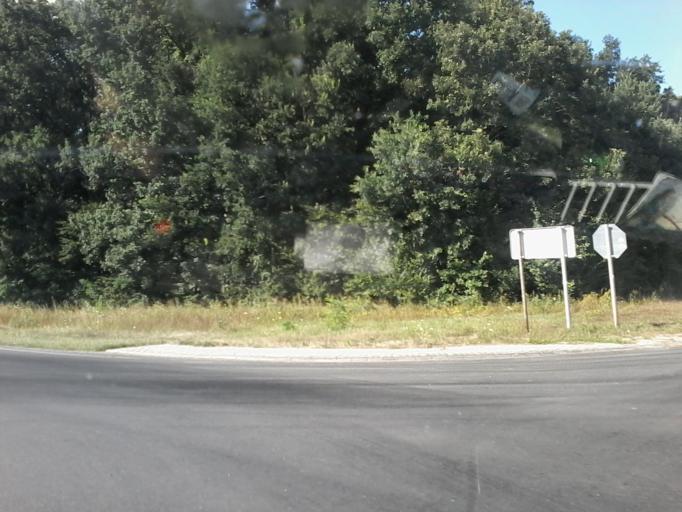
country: HU
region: Vas
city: Janoshaza
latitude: 47.1021
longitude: 17.1537
